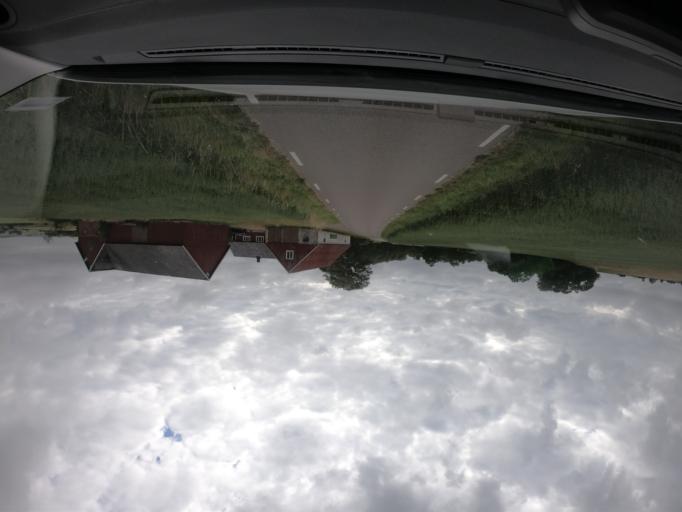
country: SE
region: Skane
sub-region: Bastads Kommun
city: Forslov
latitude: 56.3341
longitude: 12.8200
